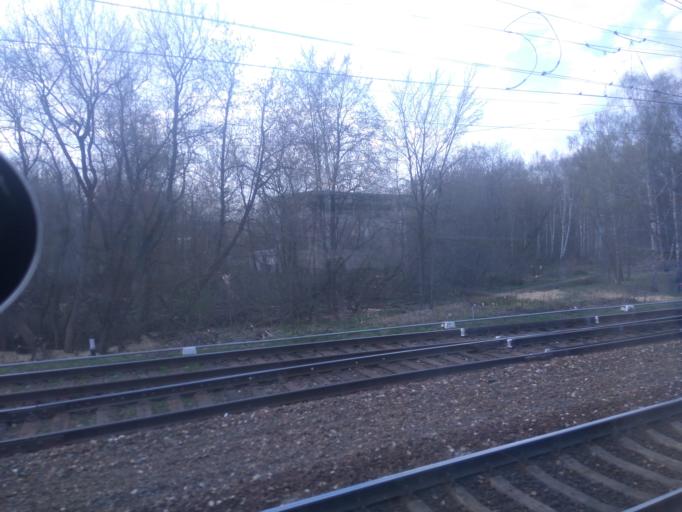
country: RU
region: Moskovskaya
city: Yakhroma
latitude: 56.2924
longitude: 37.4979
